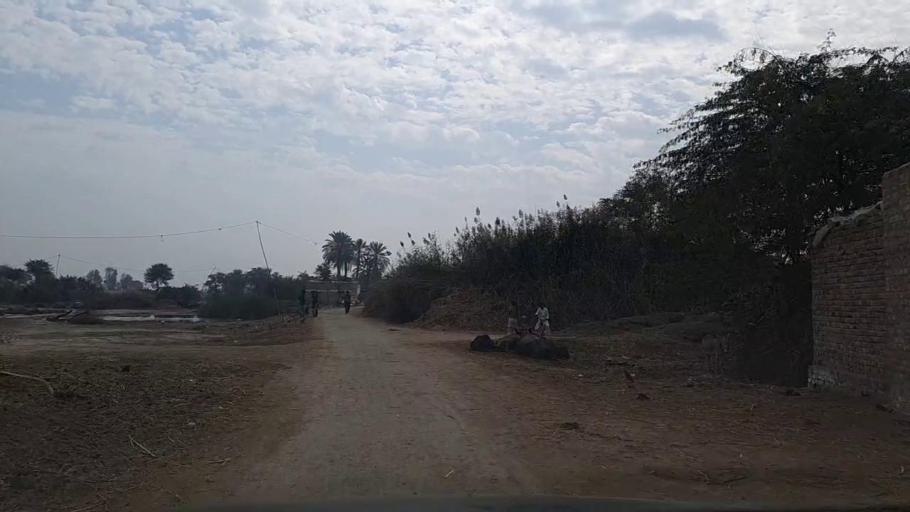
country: PK
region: Sindh
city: Daur
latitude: 26.3908
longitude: 68.3600
